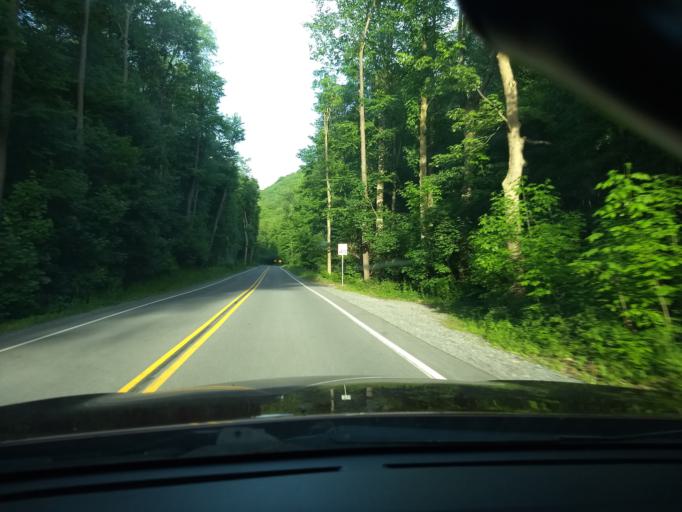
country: US
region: Pennsylvania
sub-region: Cambria County
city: Gallitzin
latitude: 40.4960
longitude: -78.4929
